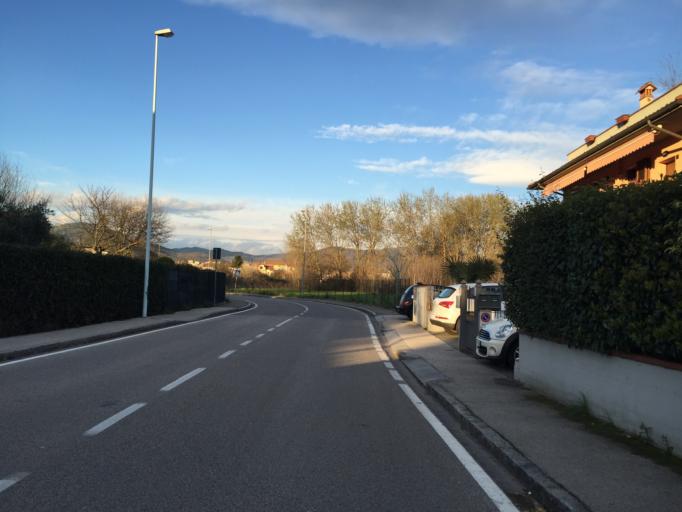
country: IT
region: Tuscany
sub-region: Provincia di Prato
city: Prato
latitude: 43.8830
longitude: 11.0550
